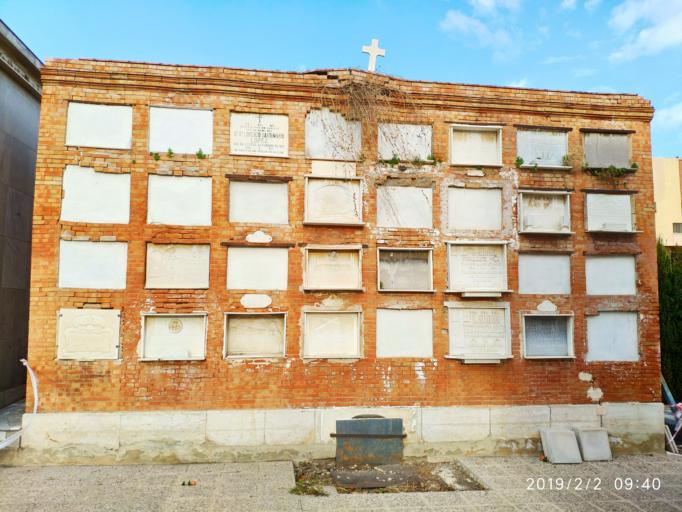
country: ES
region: Andalusia
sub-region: Provincia de Malaga
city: Malaga
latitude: 36.7347
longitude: -4.4180
